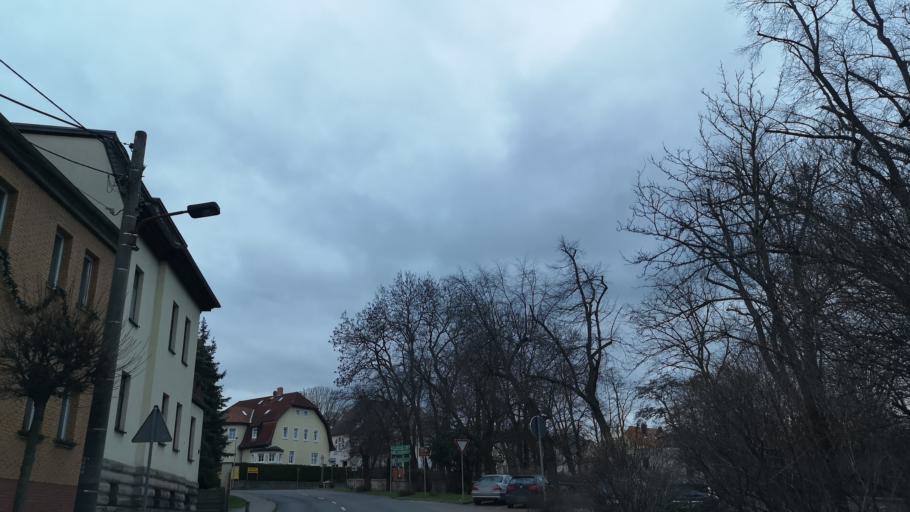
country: DE
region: Saxony-Anhalt
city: Mucheln
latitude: 51.3016
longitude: 11.8071
